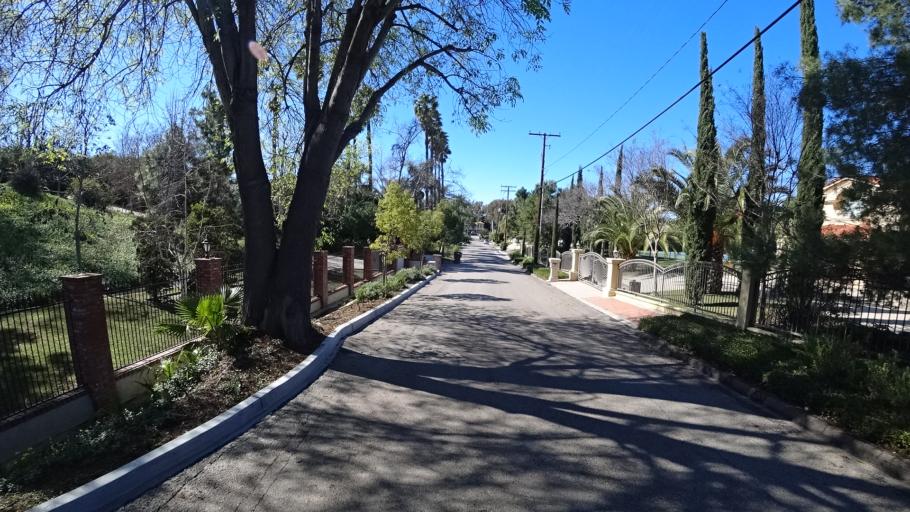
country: US
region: California
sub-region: Orange County
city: Villa Park
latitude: 33.8462
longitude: -117.8163
